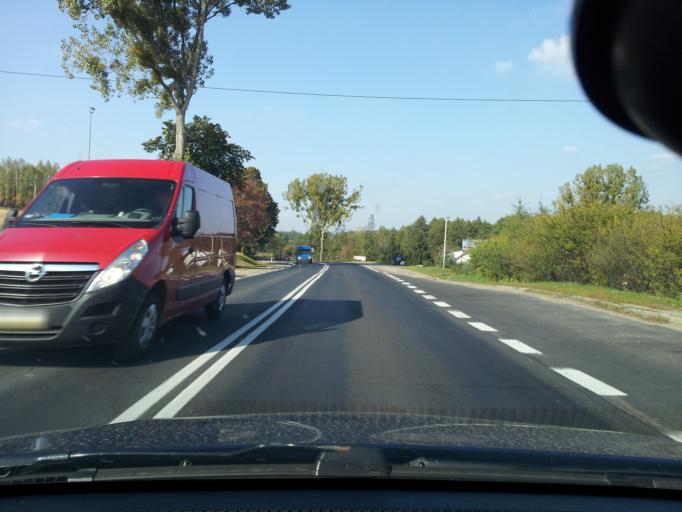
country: PL
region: Kujawsko-Pomorskie
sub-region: Powiat wloclawski
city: Fabianki
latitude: 52.7858
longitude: 19.1189
